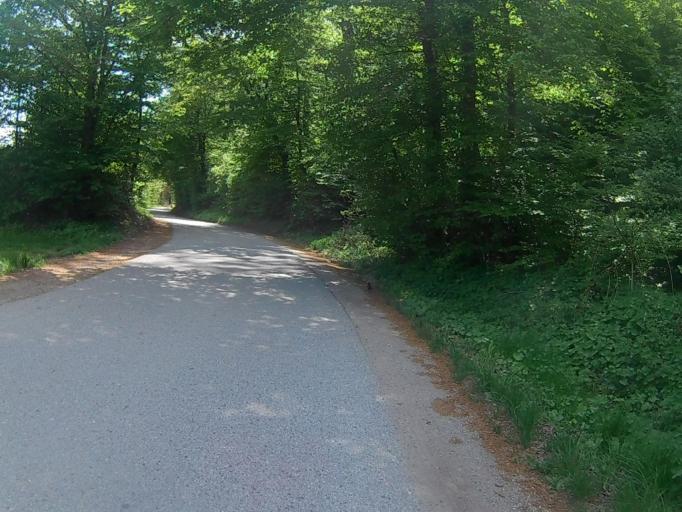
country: SI
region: Maribor
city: Pekre
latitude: 46.5490
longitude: 15.6104
